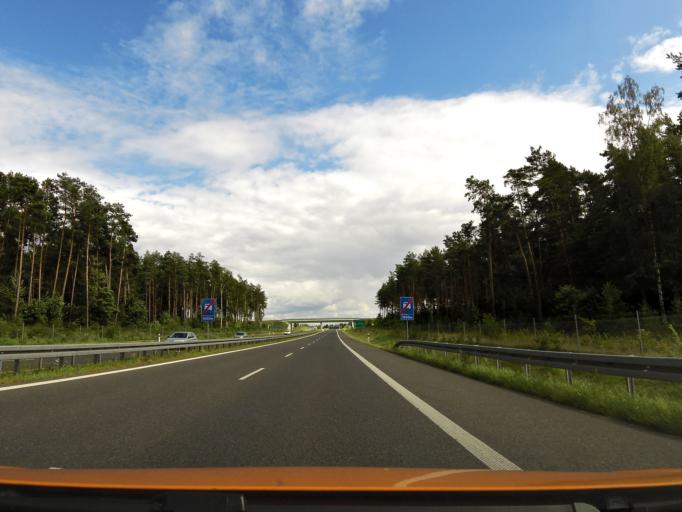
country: PL
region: West Pomeranian Voivodeship
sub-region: Powiat goleniowski
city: Nowogard
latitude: 53.6936
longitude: 15.1221
